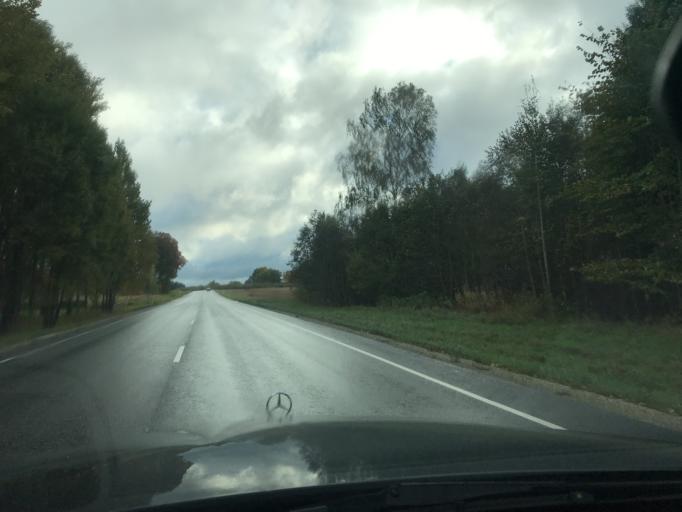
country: EE
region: Viljandimaa
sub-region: Karksi vald
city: Karksi-Nuia
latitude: 58.0107
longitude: 25.7059
